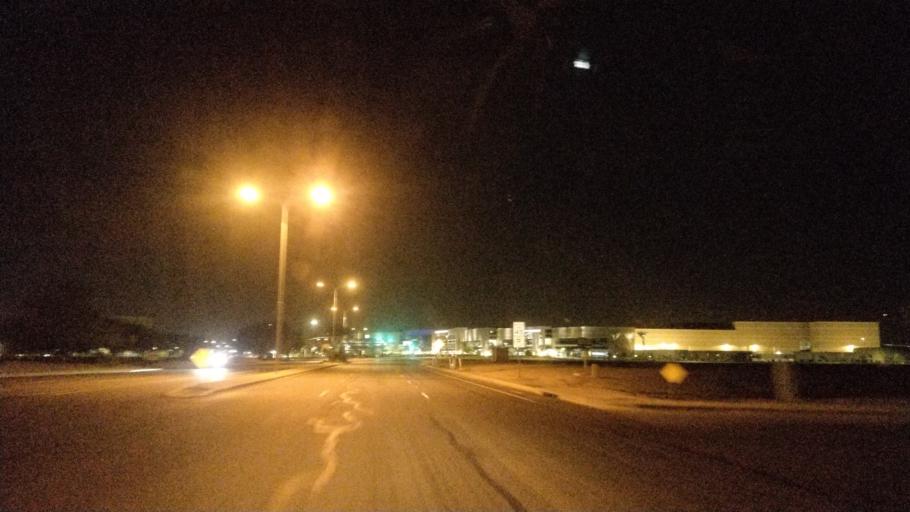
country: US
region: Arizona
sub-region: Maricopa County
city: Chandler
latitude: 33.2776
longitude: -111.8892
